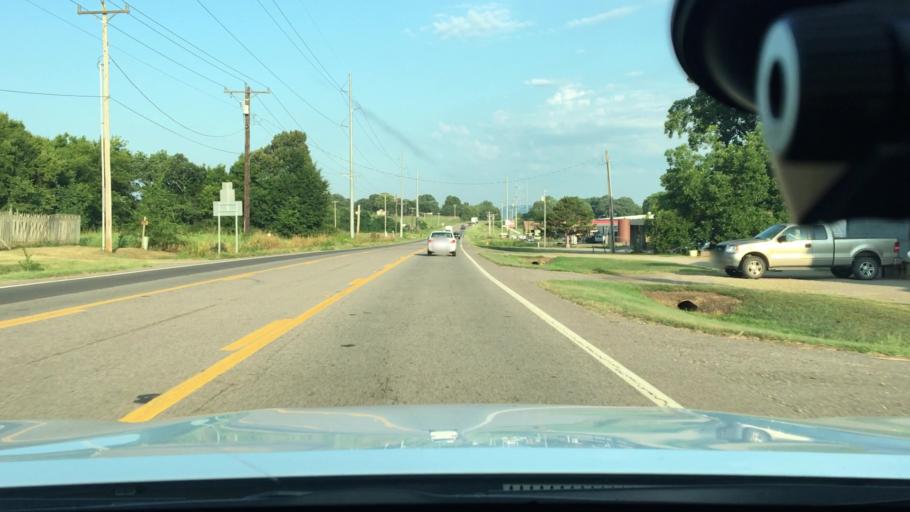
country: US
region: Arkansas
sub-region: Logan County
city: Paris
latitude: 35.2936
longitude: -93.6391
